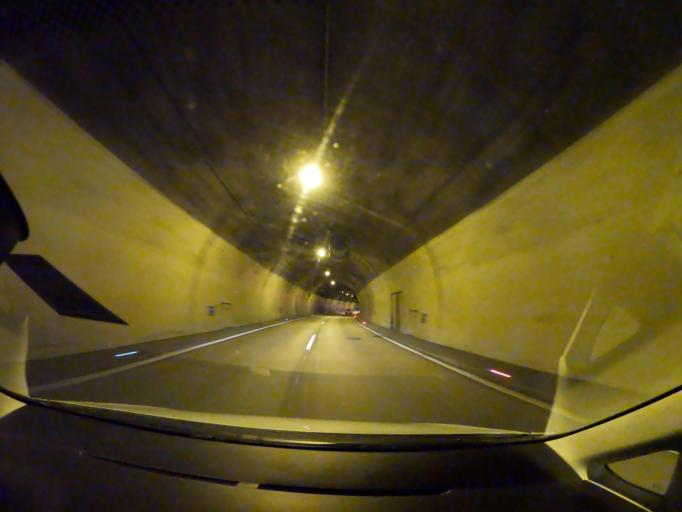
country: AT
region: Styria
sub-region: Politischer Bezirk Voitsberg
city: Modriach
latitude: 46.9747
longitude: 15.0866
